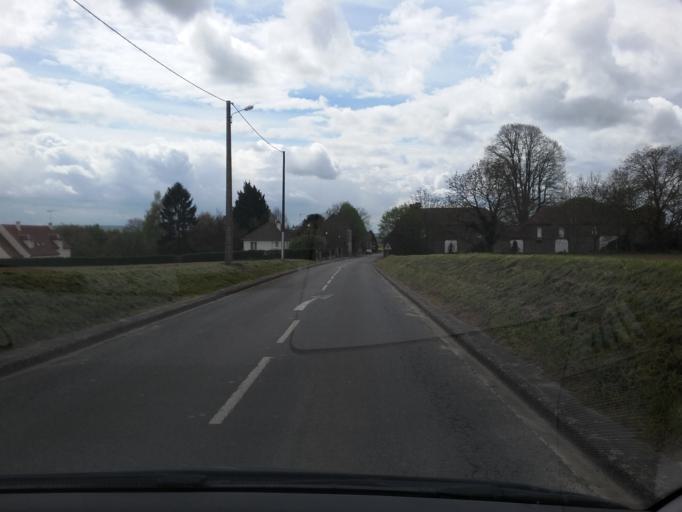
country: FR
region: Picardie
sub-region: Departement de l'Oise
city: Grandfresnoy
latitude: 49.3661
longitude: 2.6443
